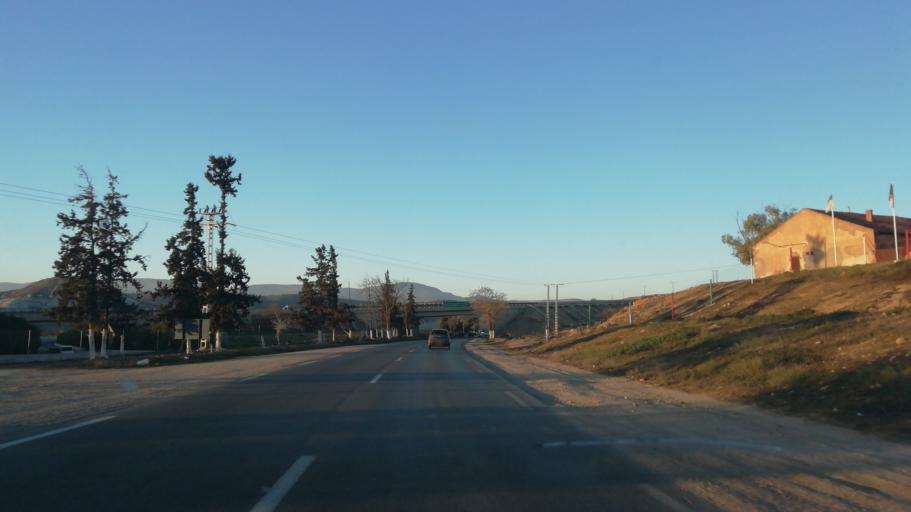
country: DZ
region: Tlemcen
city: Nedroma
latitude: 34.8991
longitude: -1.6389
